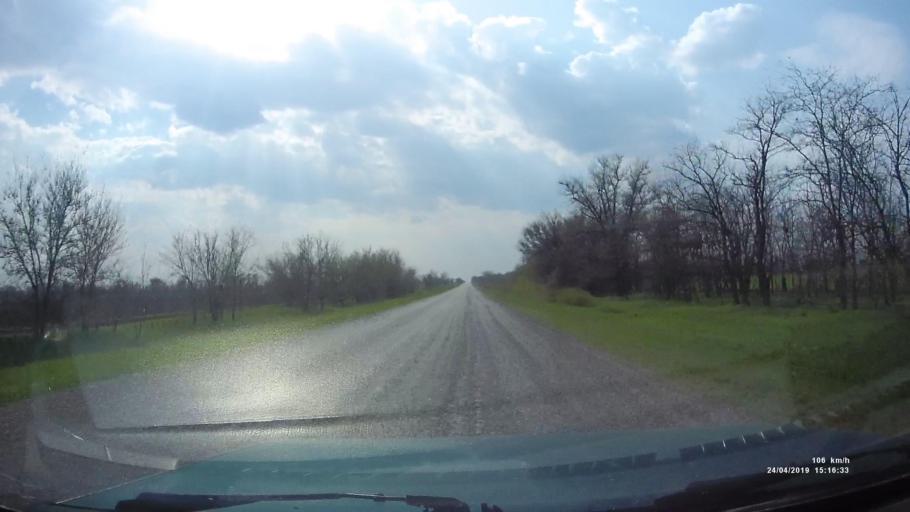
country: RU
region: Rostov
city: Remontnoye
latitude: 46.5465
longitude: 43.2104
